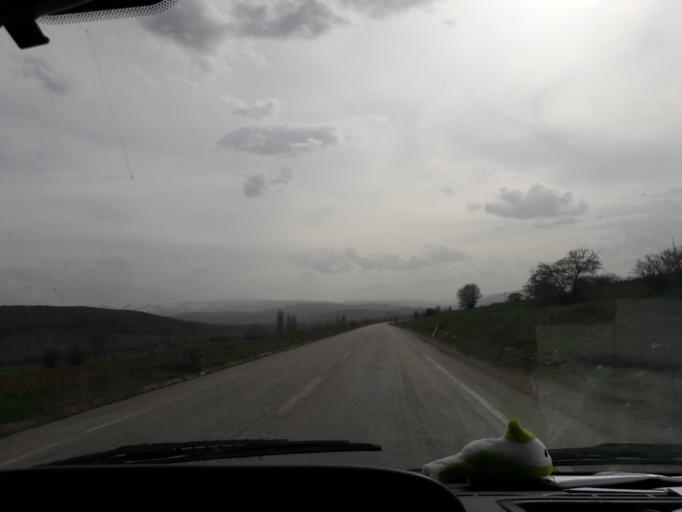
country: TR
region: Gumushane
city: Siran
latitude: 40.1744
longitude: 39.0855
